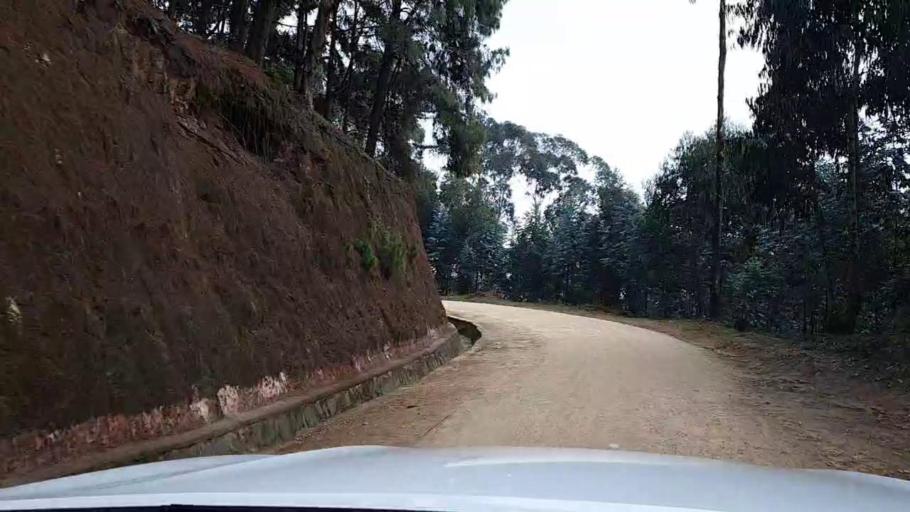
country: RW
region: Southern Province
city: Nzega
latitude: -2.3809
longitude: 29.3830
